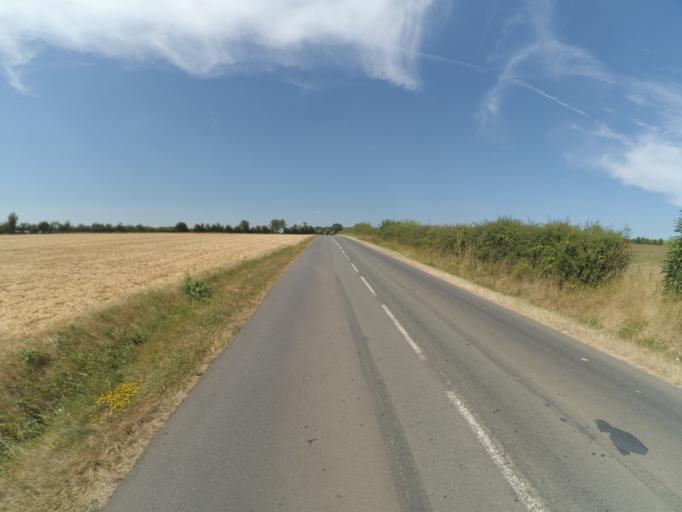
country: FR
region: Poitou-Charentes
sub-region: Departement de la Vienne
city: La Villedieu-du-Clain
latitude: 46.4021
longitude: 0.3450
